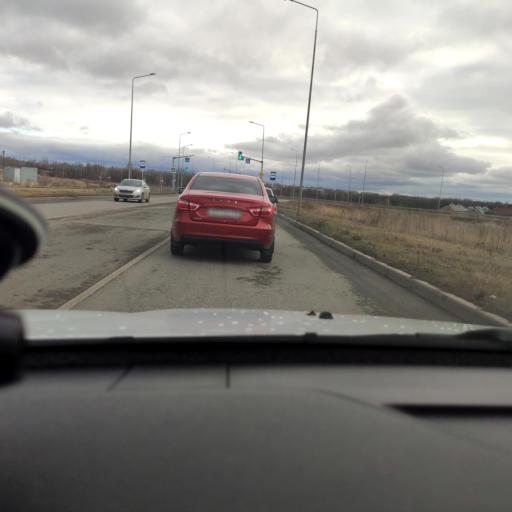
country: RU
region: Samara
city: Petra-Dubrava
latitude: 53.3092
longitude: 50.3497
